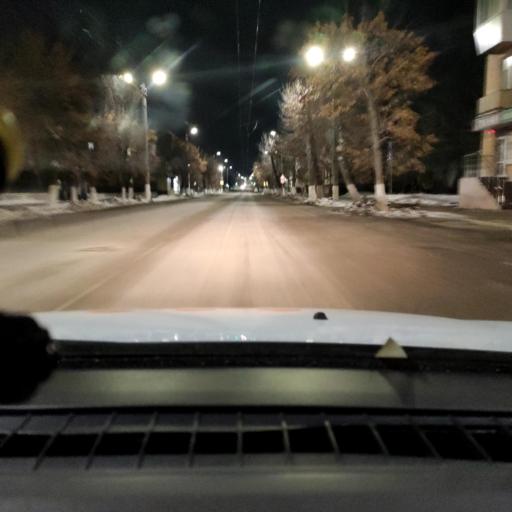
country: RU
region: Samara
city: Novokuybyshevsk
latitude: 53.0945
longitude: 49.9494
